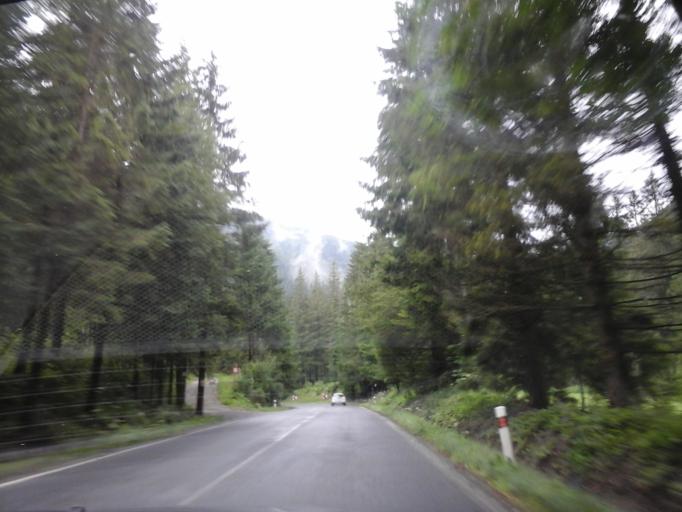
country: SK
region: Presovsky
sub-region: Okres Poprad
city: Zdiar
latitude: 49.2477
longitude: 20.3107
